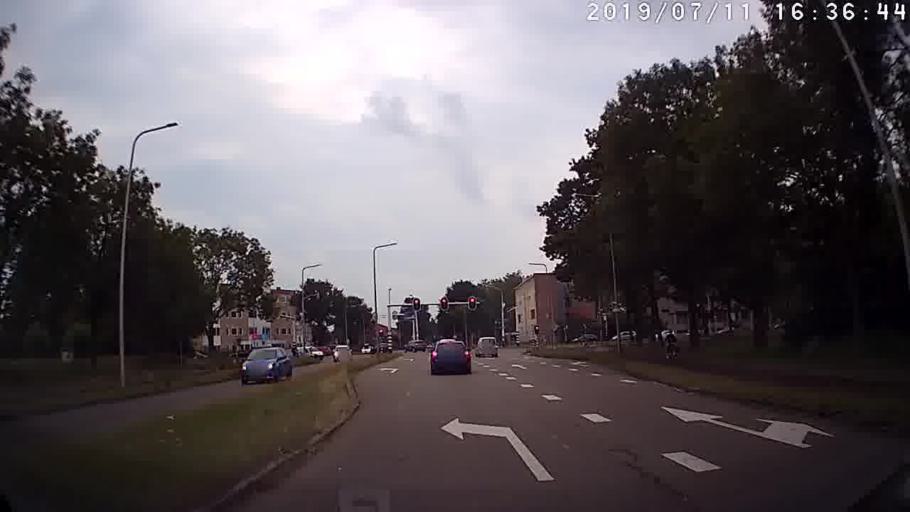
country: NL
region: Overijssel
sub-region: Gemeente Zwolle
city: Zwolle
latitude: 52.5056
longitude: 6.1143
